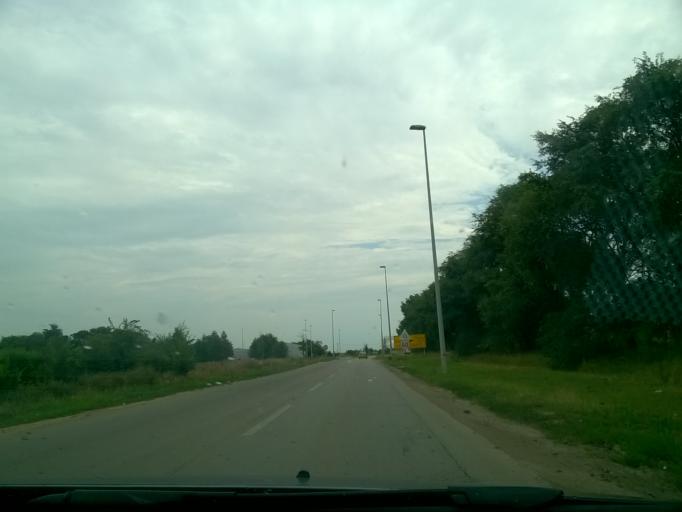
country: RS
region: Autonomna Pokrajina Vojvodina
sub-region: Srednjebanatski Okrug
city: Zrenjanin
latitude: 45.4020
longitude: 20.3911
